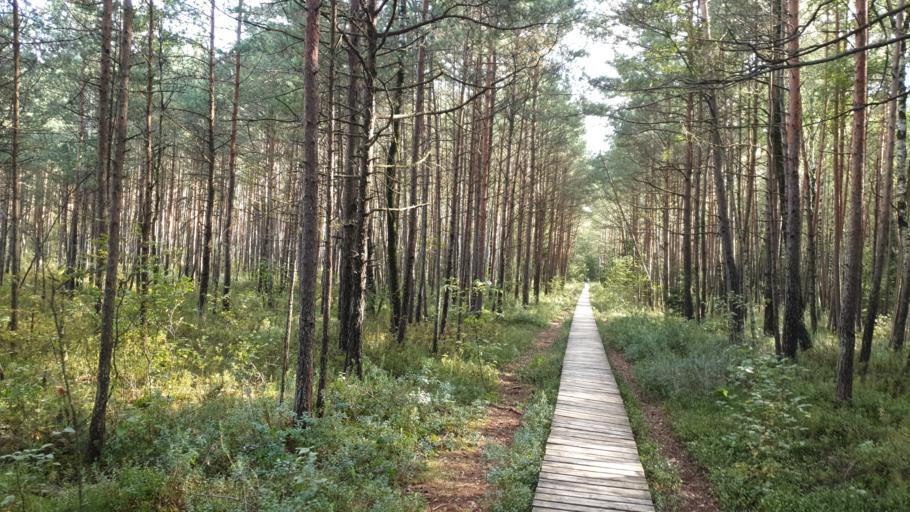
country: LT
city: Trakai
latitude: 54.6414
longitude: 24.9684
